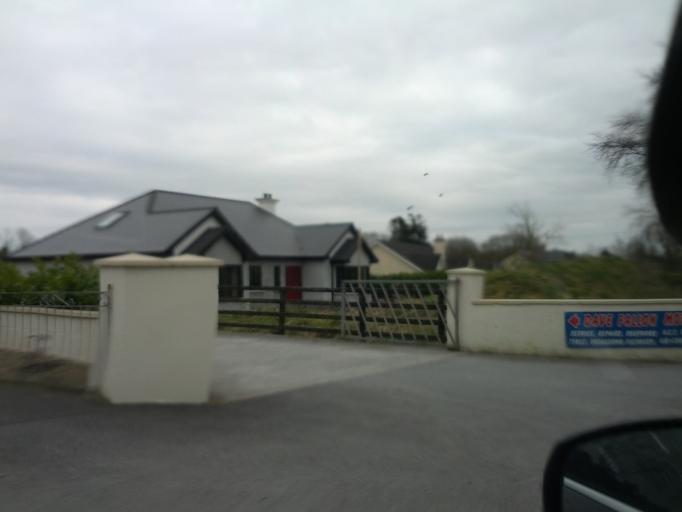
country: IE
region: Connaught
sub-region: County Galway
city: Athenry
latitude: 53.2417
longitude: -8.7483
